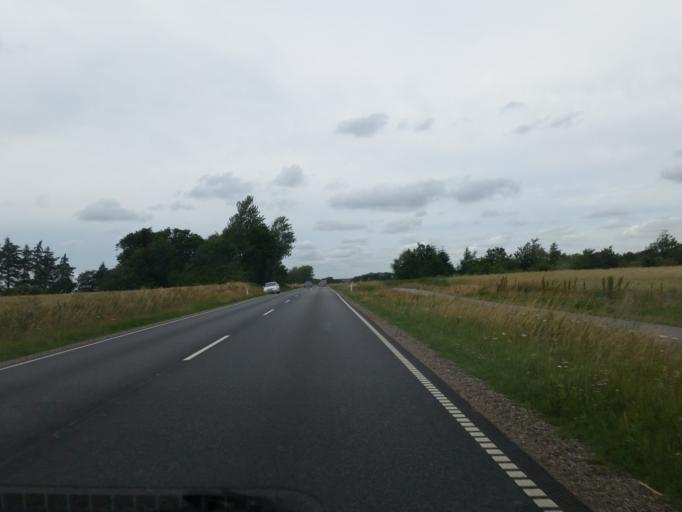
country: DK
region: South Denmark
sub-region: Esbjerg Kommune
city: Ribe
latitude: 55.2590
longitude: 8.7224
